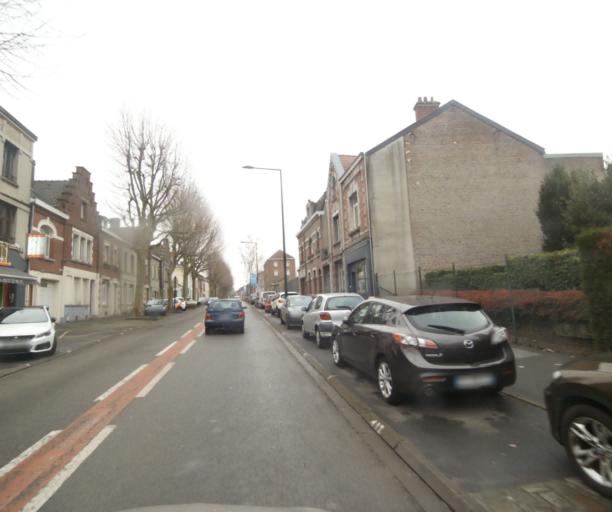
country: FR
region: Nord-Pas-de-Calais
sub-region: Departement du Nord
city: Valenciennes
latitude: 50.3477
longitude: 3.5248
